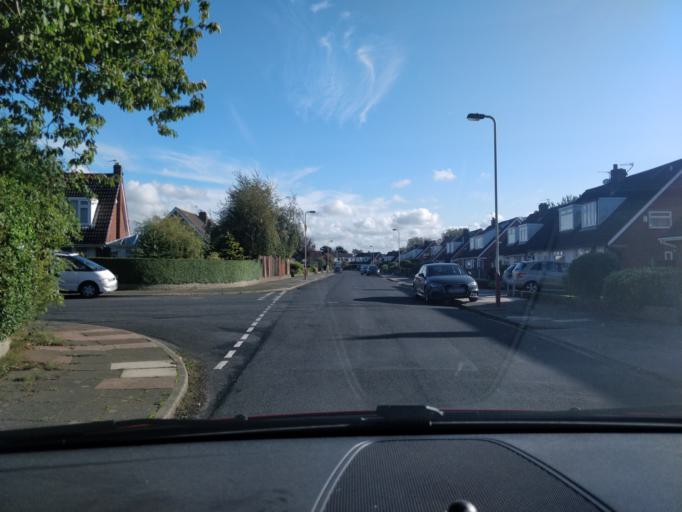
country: GB
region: England
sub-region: Lancashire
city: Banks
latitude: 53.6789
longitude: -2.9504
